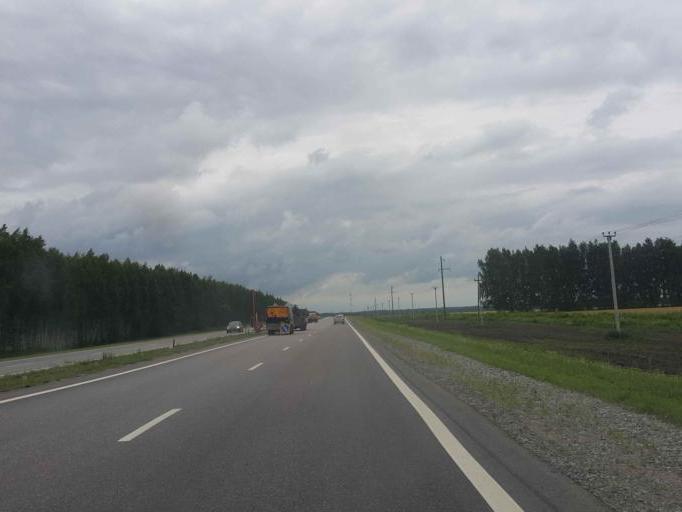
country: RU
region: Tambov
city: Zavoronezhskoye
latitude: 52.8827
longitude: 40.7283
